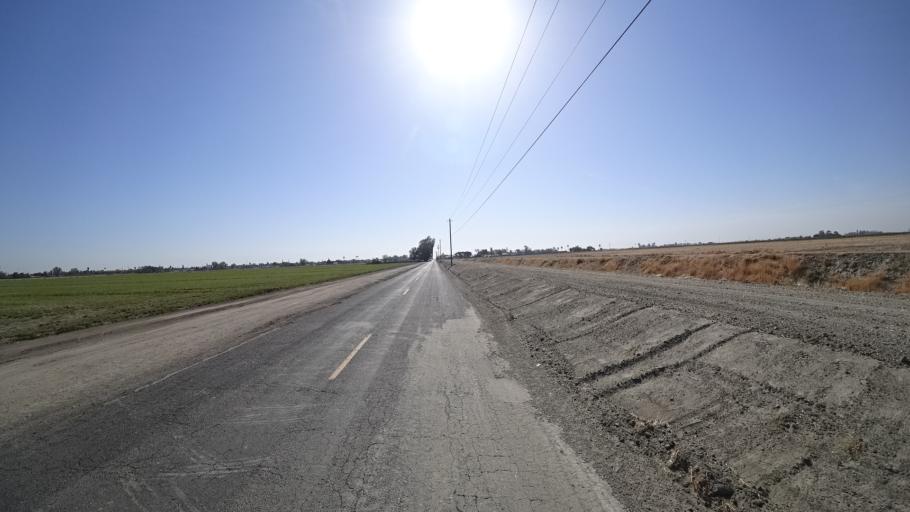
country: US
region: California
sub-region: Kings County
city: Corcoran
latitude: 36.0835
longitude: -119.5807
